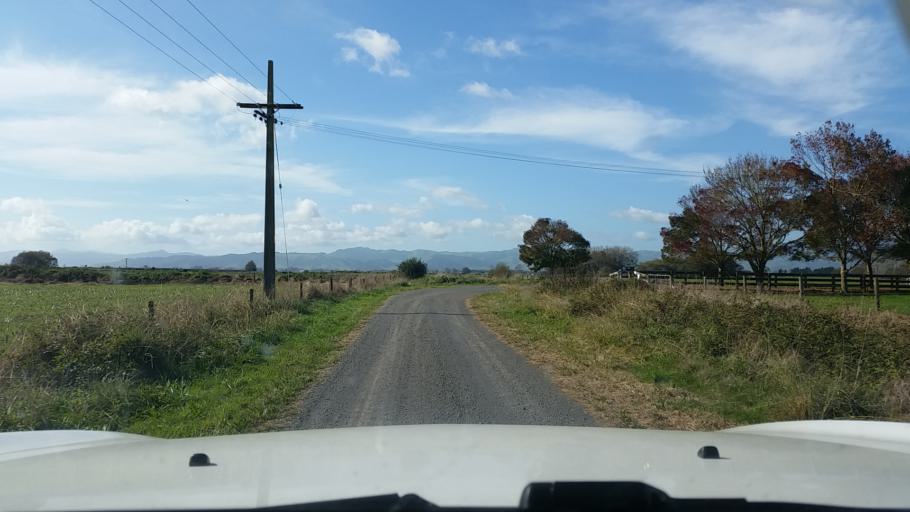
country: NZ
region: Waikato
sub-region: Hauraki District
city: Paeroa
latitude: -37.4995
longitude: 175.5651
